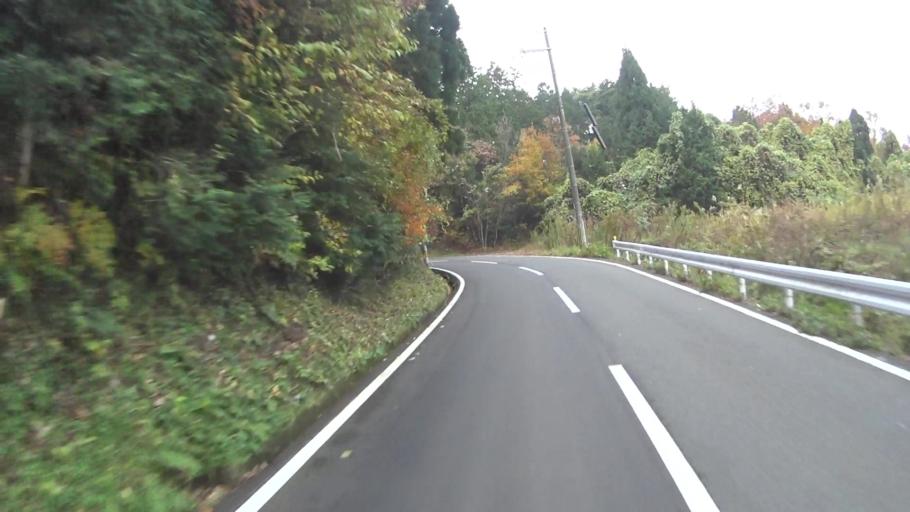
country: JP
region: Kyoto
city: Maizuru
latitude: 35.5516
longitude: 135.4520
